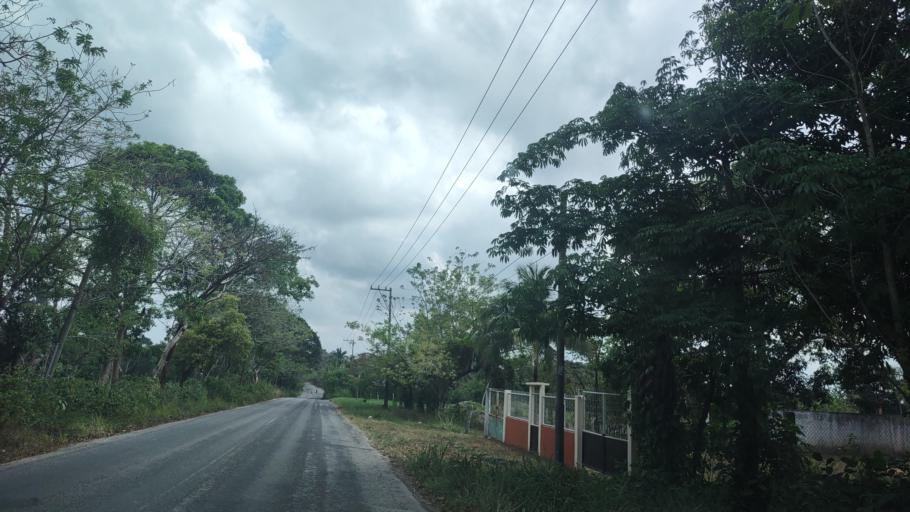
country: MX
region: Veracruz
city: Las Choapas
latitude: 17.9518
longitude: -94.1099
